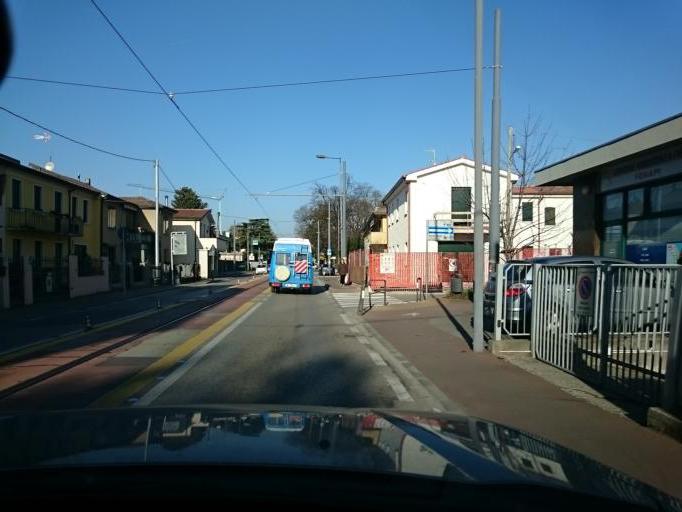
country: IT
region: Veneto
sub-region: Provincia di Padova
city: Mandriola-Sant'Agostino
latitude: 45.3816
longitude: 11.8691
